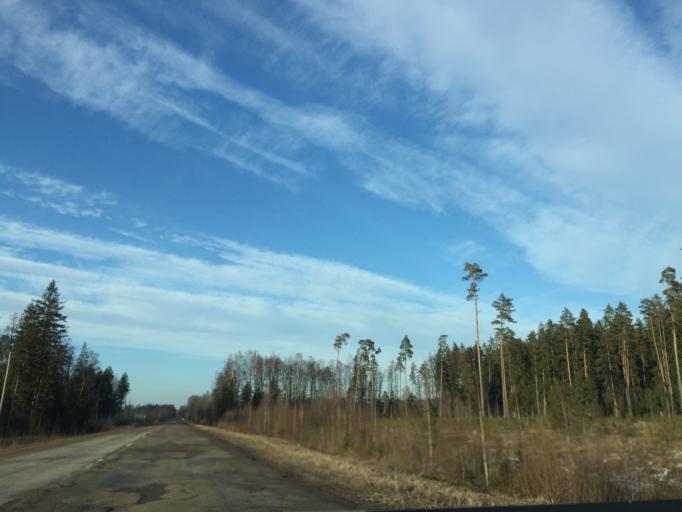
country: LV
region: Kekava
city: Balozi
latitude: 56.7268
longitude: 24.1104
